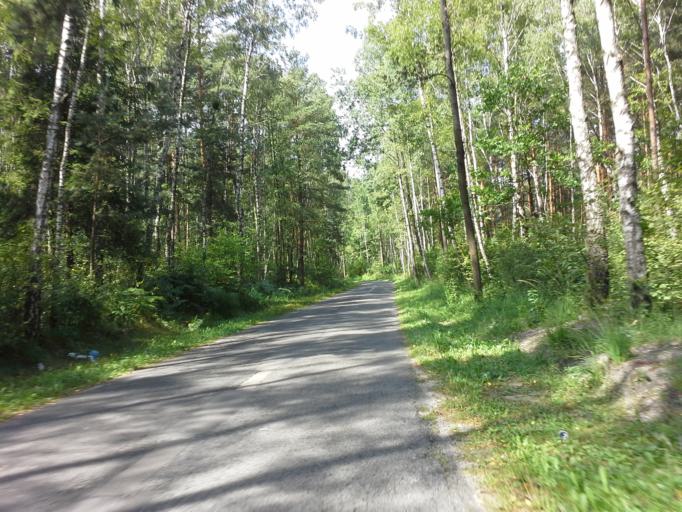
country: PL
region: Lesser Poland Voivodeship
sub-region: Powiat chrzanowski
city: Trzebinia
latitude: 50.1404
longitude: 19.4502
